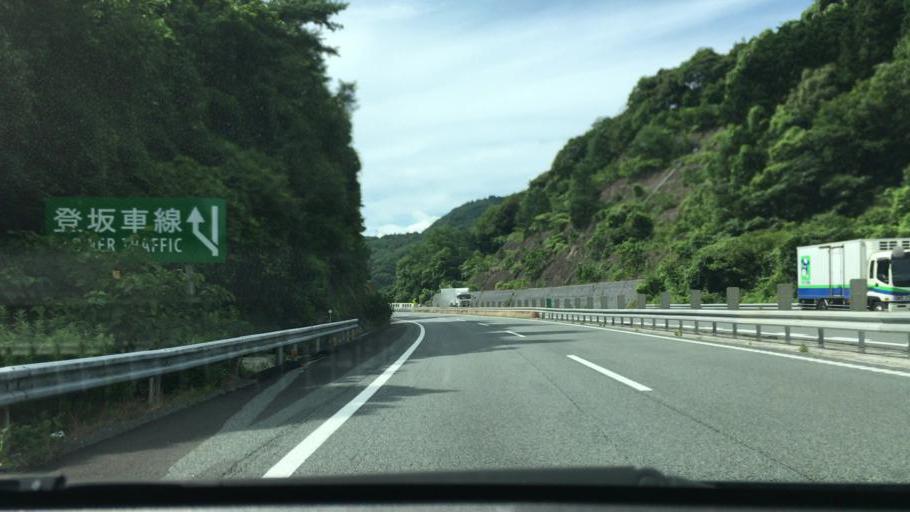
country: JP
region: Yamaguchi
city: Ogori-shimogo
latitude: 34.1352
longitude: 131.3747
